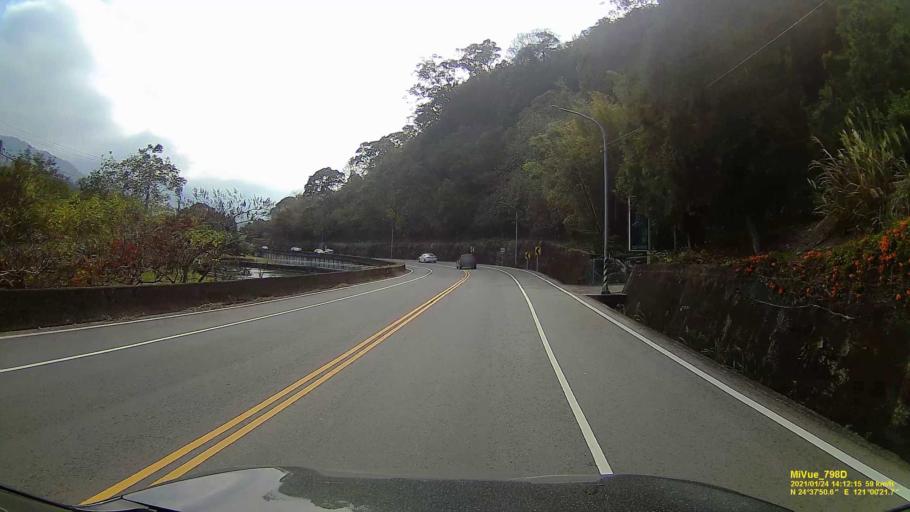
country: TW
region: Taiwan
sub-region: Hsinchu
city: Hsinchu
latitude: 24.6304
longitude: 121.0058
